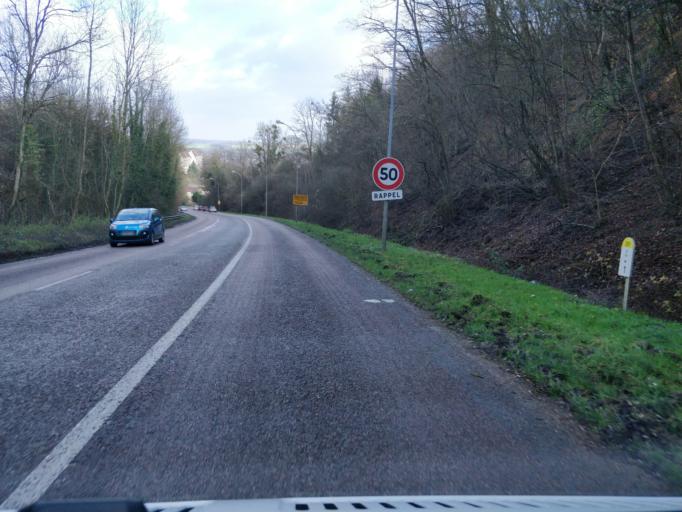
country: FR
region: Bourgogne
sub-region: Departement de l'Yonne
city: Paron
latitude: 48.1922
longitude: 3.2543
